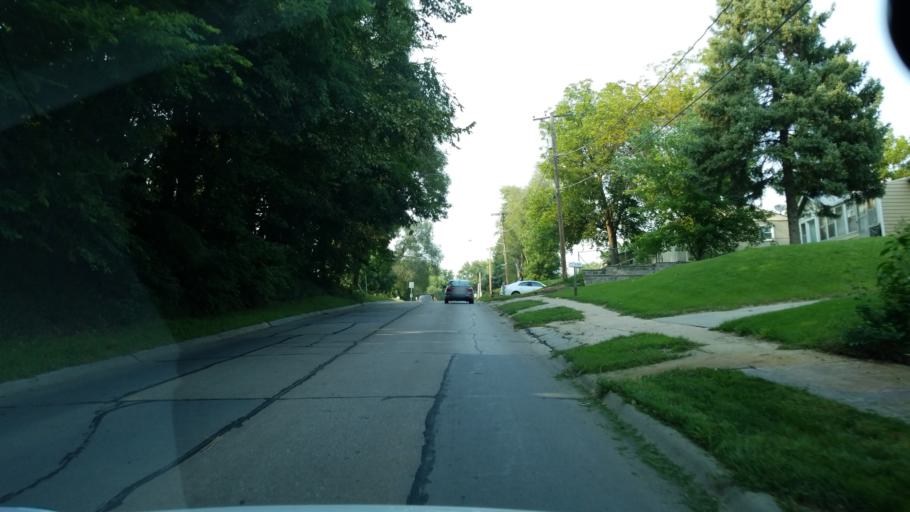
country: US
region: Nebraska
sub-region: Sarpy County
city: Bellevue
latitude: 41.1296
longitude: -95.8924
